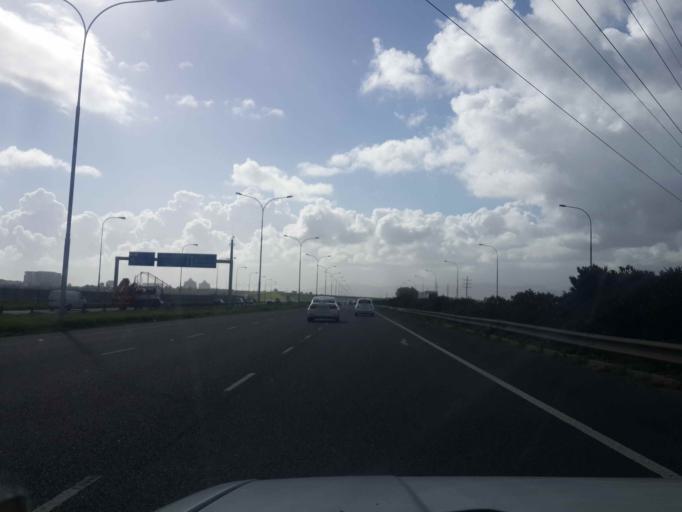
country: ZA
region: Western Cape
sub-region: City of Cape Town
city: Sunset Beach
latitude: -33.9066
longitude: 18.5034
